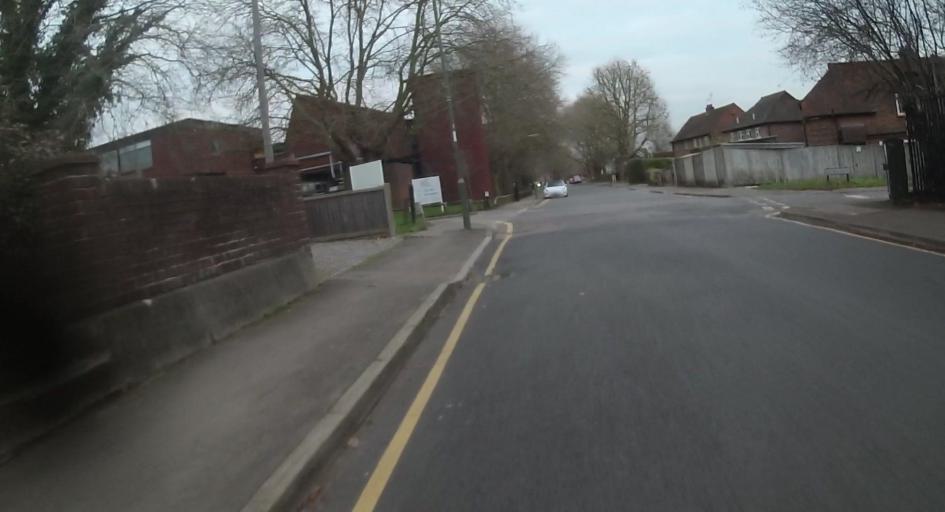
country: GB
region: England
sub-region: Surrey
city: Farnham
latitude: 51.2148
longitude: -0.8069
